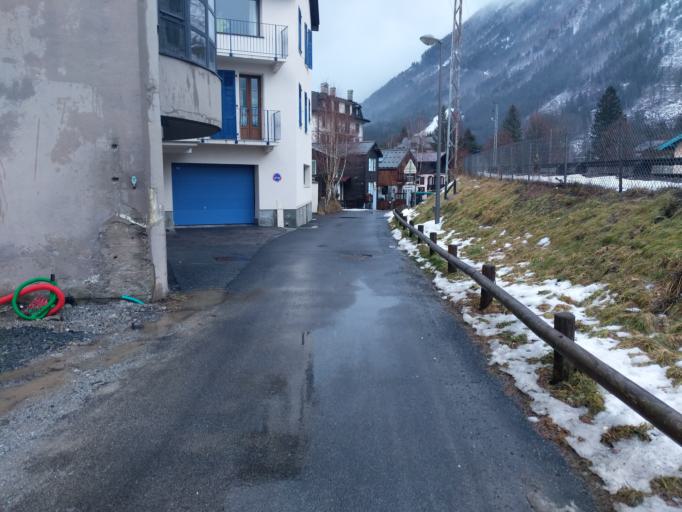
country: FR
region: Rhone-Alpes
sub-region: Departement de la Haute-Savoie
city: Chamonix-Mont-Blanc
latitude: 45.9207
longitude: 6.8675
